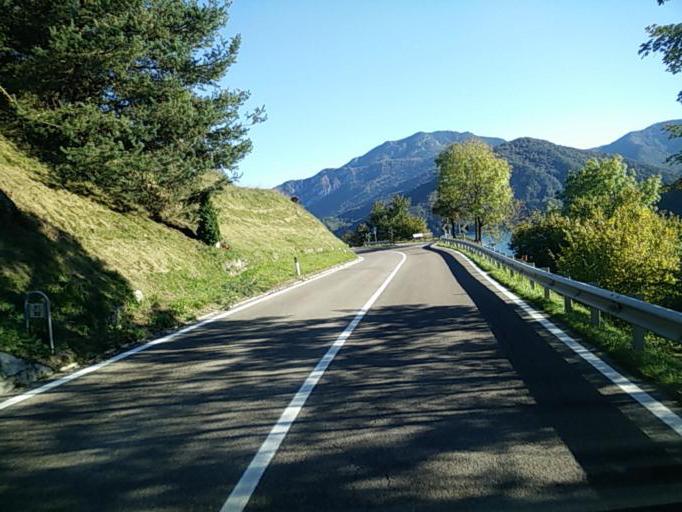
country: IT
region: Trentino-Alto Adige
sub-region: Provincia di Trento
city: Pieve di Ledro
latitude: 45.8856
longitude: 10.7429
